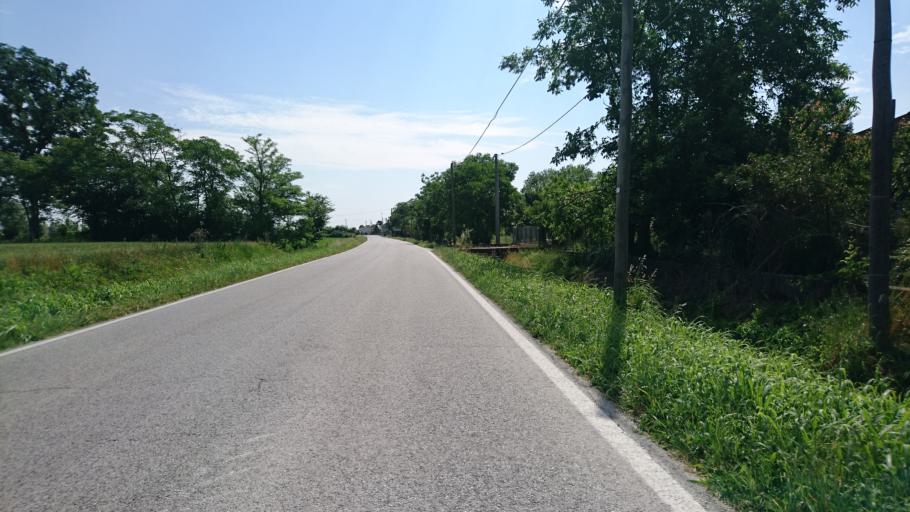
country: IT
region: Veneto
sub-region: Provincia di Padova
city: Santa Margherita d'Adige
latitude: 45.1919
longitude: 11.5515
